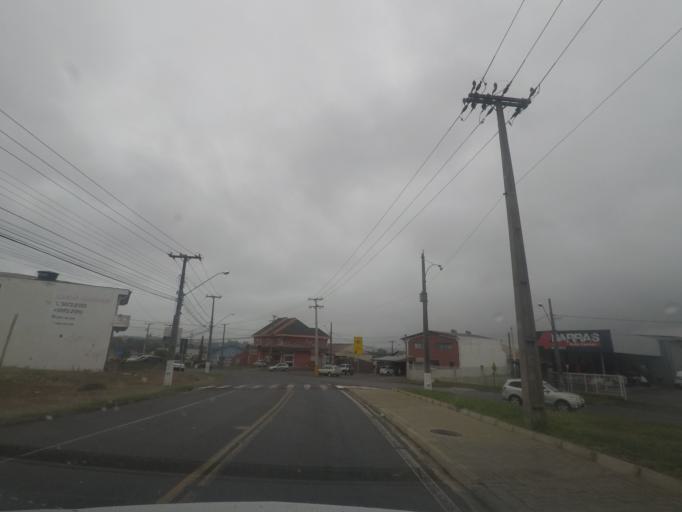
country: BR
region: Parana
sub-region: Quatro Barras
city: Quatro Barras
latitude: -25.3699
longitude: -49.0811
